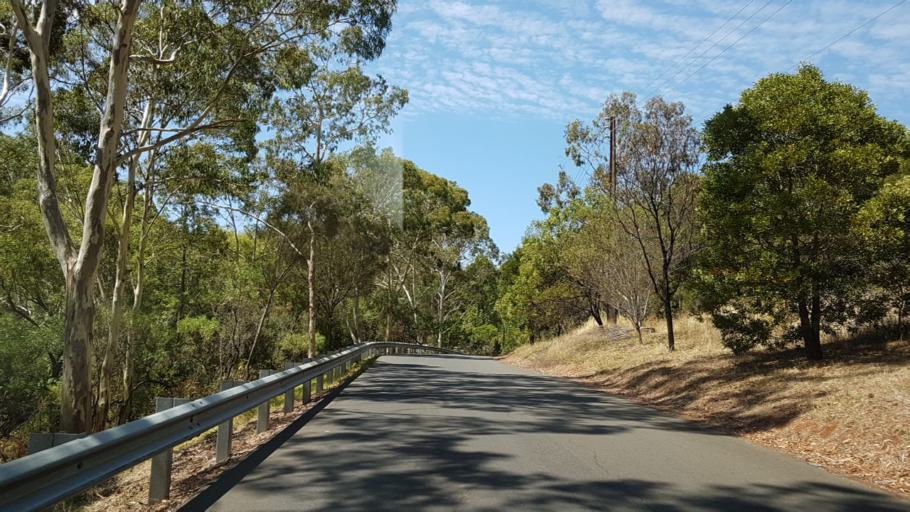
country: AU
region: South Australia
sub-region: Mitcham
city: Belair
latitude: -34.9896
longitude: 138.6378
